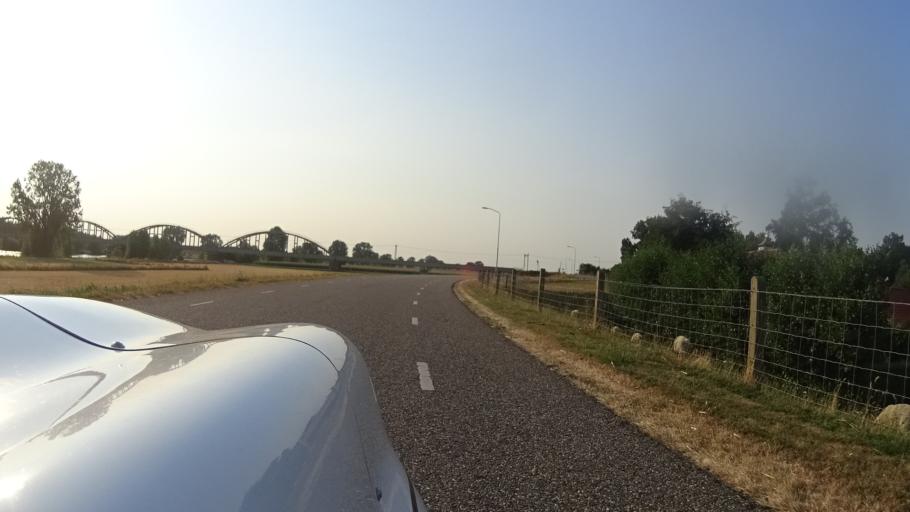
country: NL
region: Gelderland
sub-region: Gemeente Wijchen
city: Bergharen
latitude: 51.7999
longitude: 5.6587
